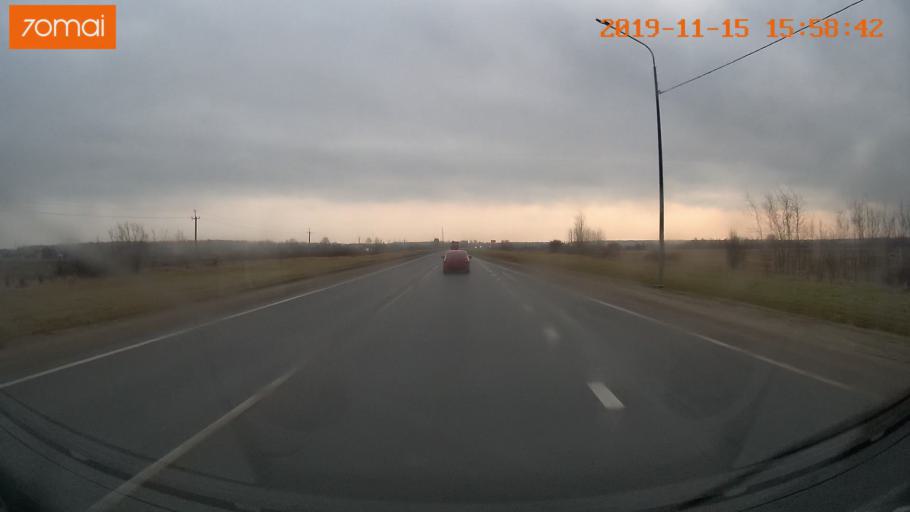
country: RU
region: Jaroslavl
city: Yaroslavl
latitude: 57.8163
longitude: 39.9530
